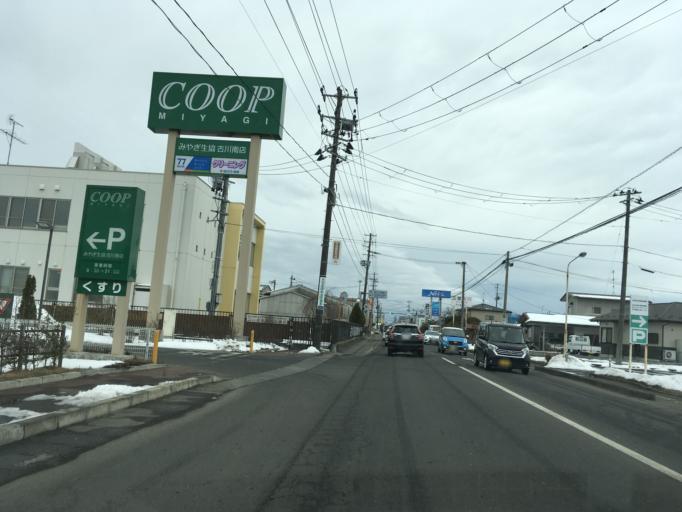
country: JP
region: Miyagi
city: Furukawa
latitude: 38.5628
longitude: 140.9540
